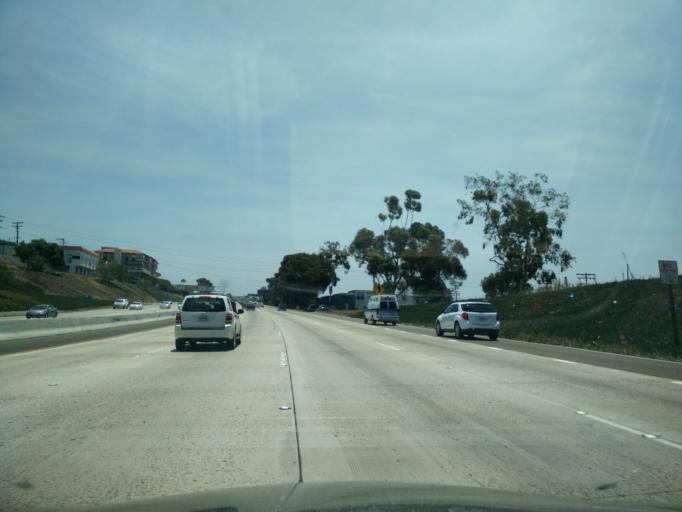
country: US
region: California
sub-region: San Diego County
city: San Diego
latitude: 32.7474
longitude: -117.1932
